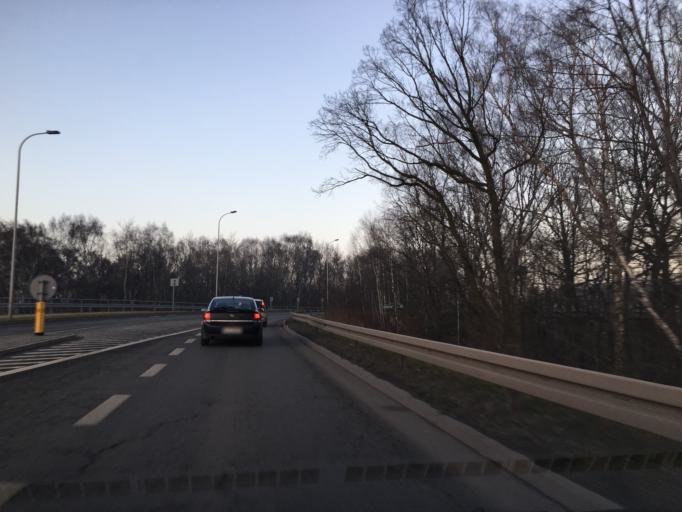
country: PL
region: Silesian Voivodeship
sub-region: Powiat tarnogorski
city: Radzionkow
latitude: 50.3691
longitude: 18.8763
